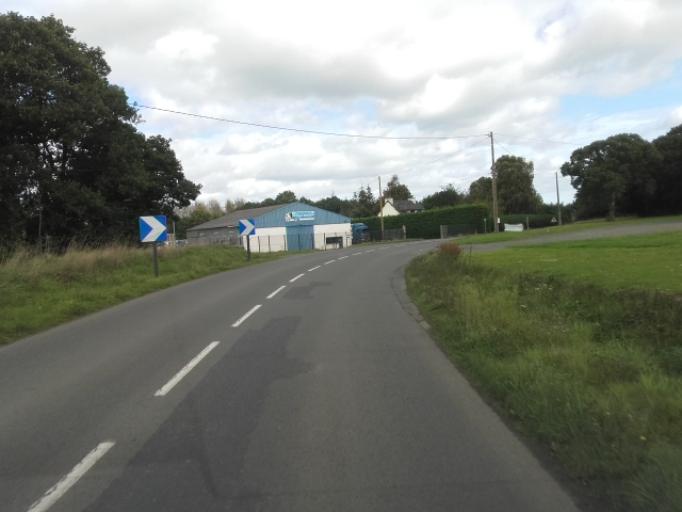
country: FR
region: Brittany
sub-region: Departement des Cotes-d'Armor
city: Lanvollon
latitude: 48.6389
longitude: -2.9749
